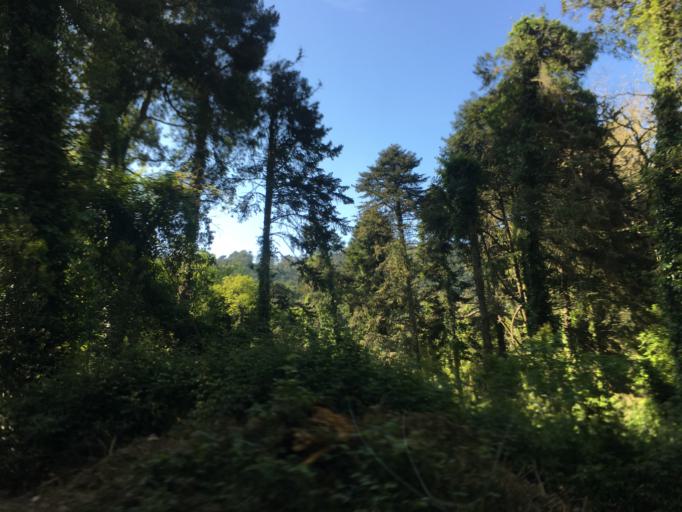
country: PT
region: Lisbon
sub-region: Sintra
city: Colares
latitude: 38.7753
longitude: -9.4613
